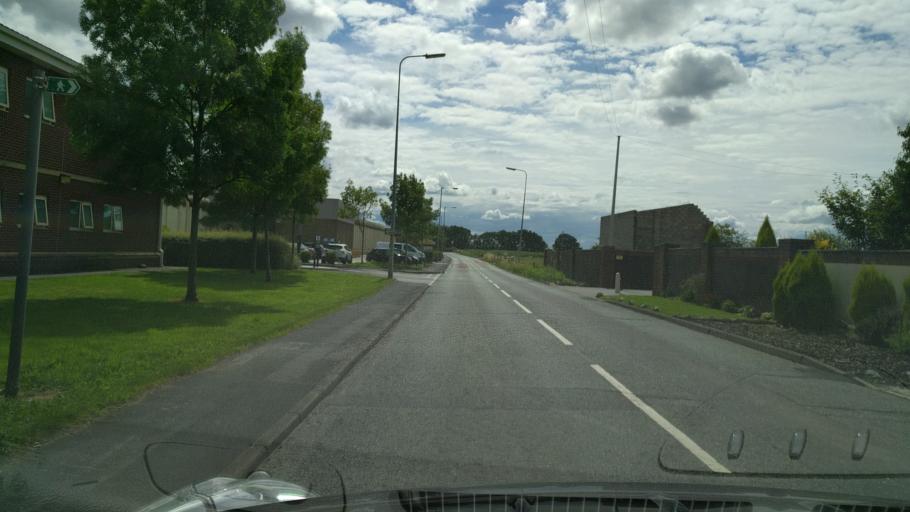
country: GB
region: England
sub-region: Warrington
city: Culcheth
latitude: 53.4397
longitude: -2.5253
